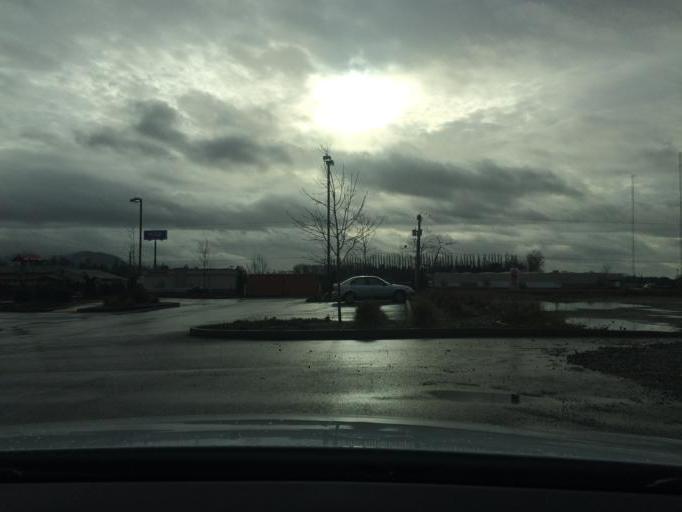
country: US
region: Washington
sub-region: Skagit County
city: Mount Vernon
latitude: 48.4401
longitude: -122.3444
